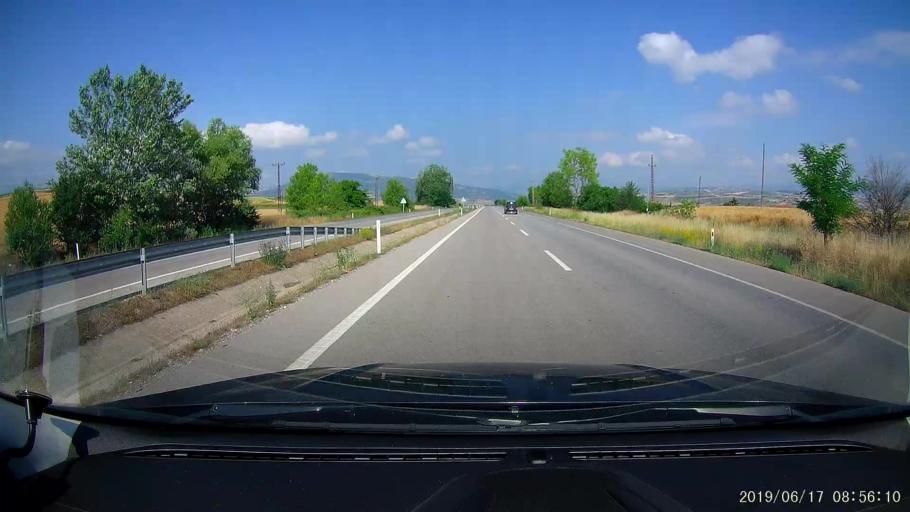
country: TR
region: Amasya
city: Esencay
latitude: 40.7333
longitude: 36.4280
